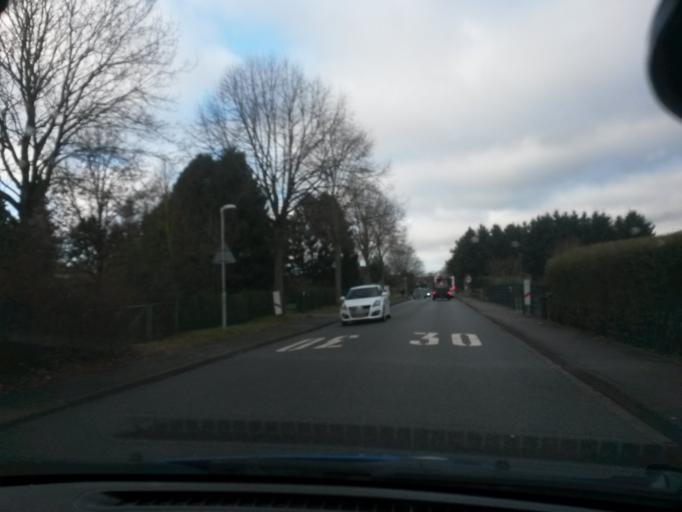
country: DE
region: Lower Saxony
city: Adendorf
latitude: 53.2630
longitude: 10.4657
